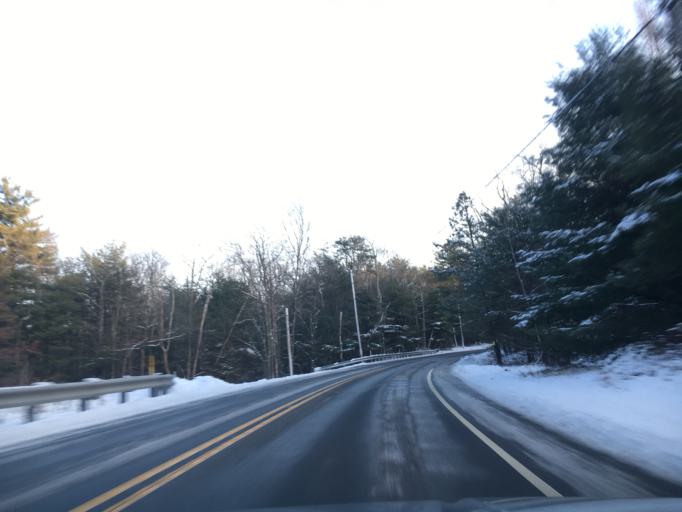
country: US
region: Pennsylvania
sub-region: Pike County
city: Hemlock Farms
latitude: 41.3210
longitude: -75.1160
